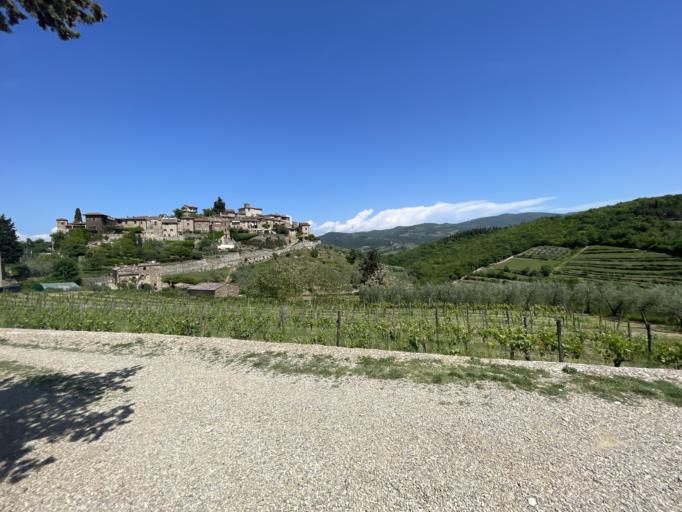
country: IT
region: Tuscany
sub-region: Province of Florence
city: Greve in Chianti
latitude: 43.5797
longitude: 11.3011
